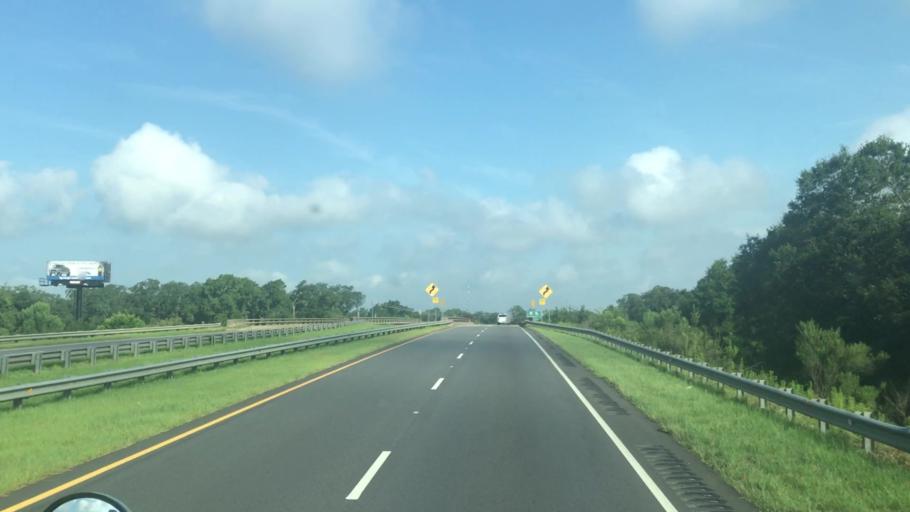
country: US
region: Georgia
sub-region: Decatur County
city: Bainbridge
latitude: 30.8961
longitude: -84.5837
